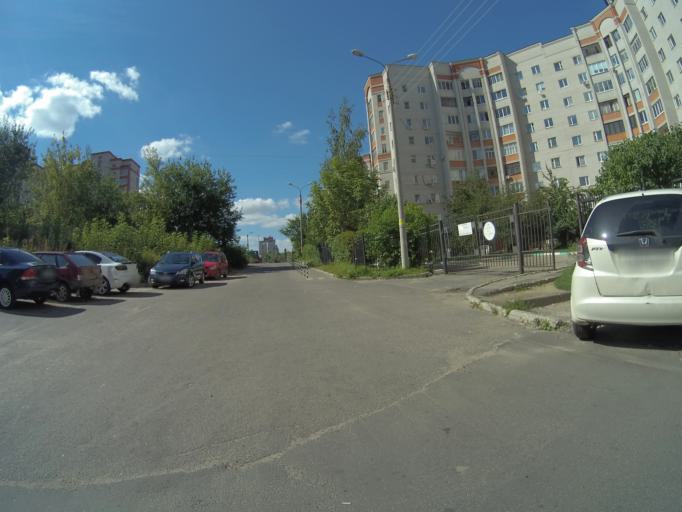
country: RU
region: Vladimir
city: Vladimir
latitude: 56.1358
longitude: 40.3761
